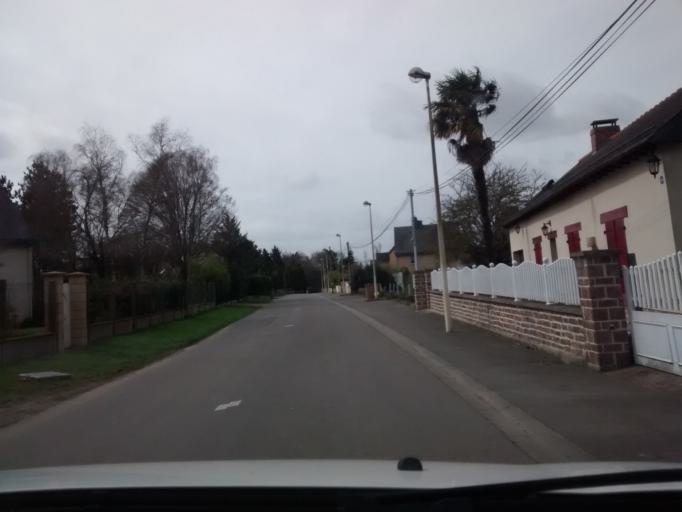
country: FR
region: Brittany
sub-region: Departement d'Ille-et-Vilaine
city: Bruz
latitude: 48.0412
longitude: -1.7499
